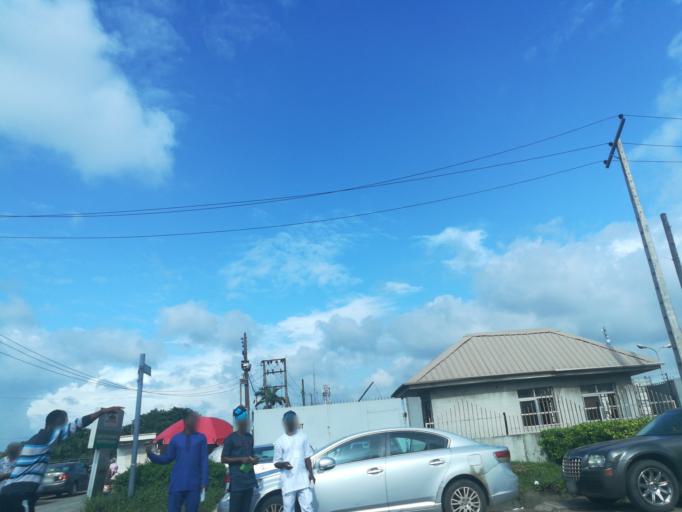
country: NG
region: Lagos
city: Ikeja
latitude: 6.6182
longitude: 3.3532
